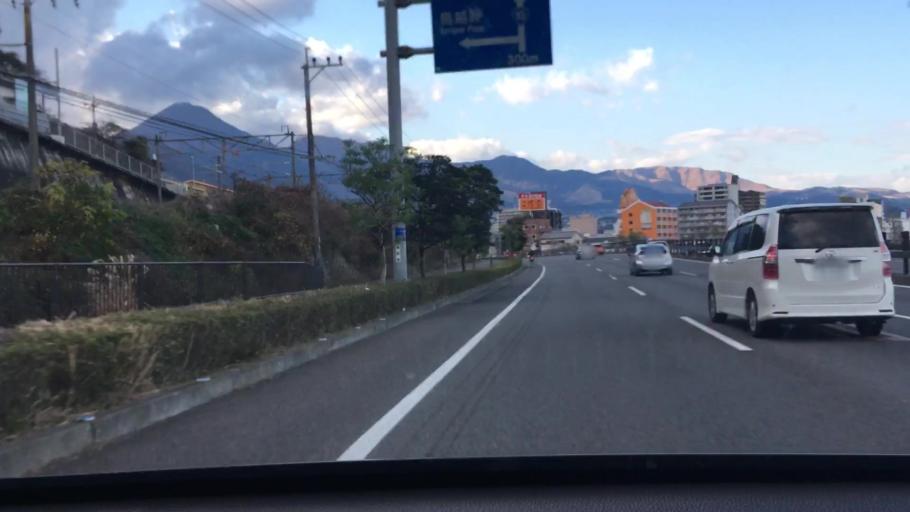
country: JP
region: Oita
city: Beppu
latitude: 33.2661
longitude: 131.5147
